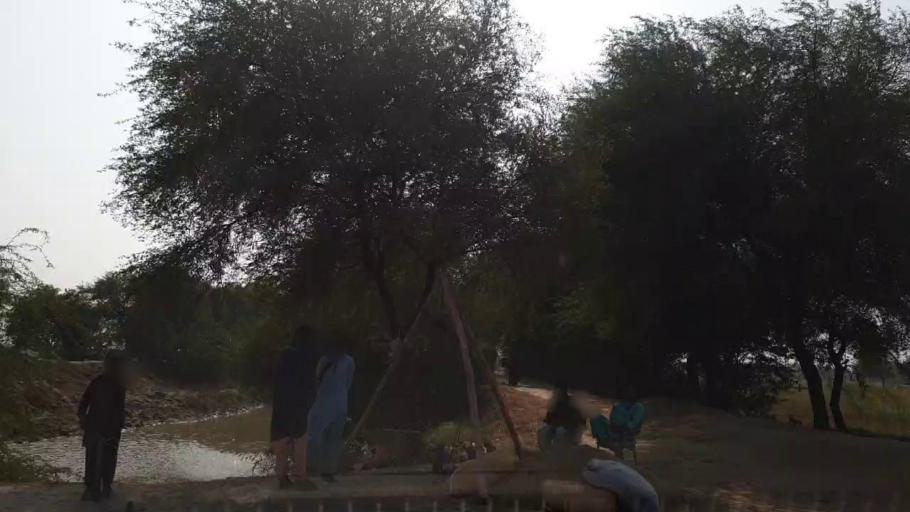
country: PK
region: Sindh
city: Kario
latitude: 24.9323
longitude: 68.5587
